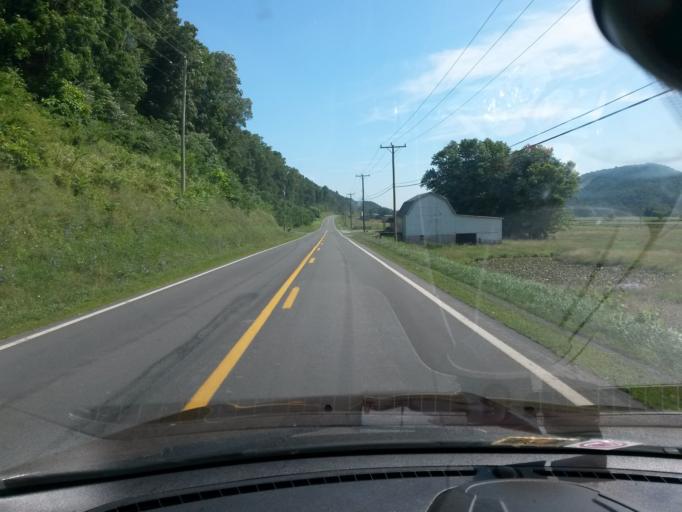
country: US
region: Virginia
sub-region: Shenandoah County
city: Basye
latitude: 39.0042
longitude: -78.7723
